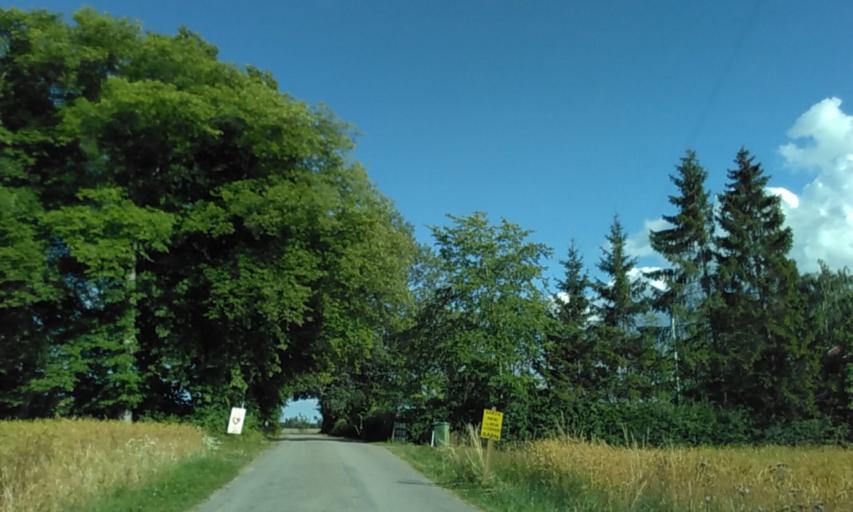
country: SE
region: Vaestra Goetaland
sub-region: Lidkopings Kommun
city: Lidkoping
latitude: 58.5746
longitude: 13.0187
